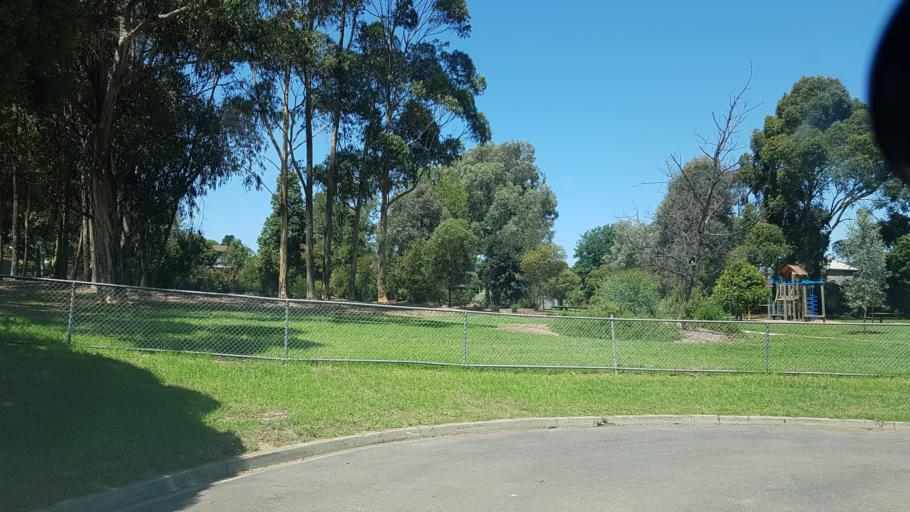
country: AU
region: Victoria
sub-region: Manningham
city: Bulleen
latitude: -37.7618
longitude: 145.0990
